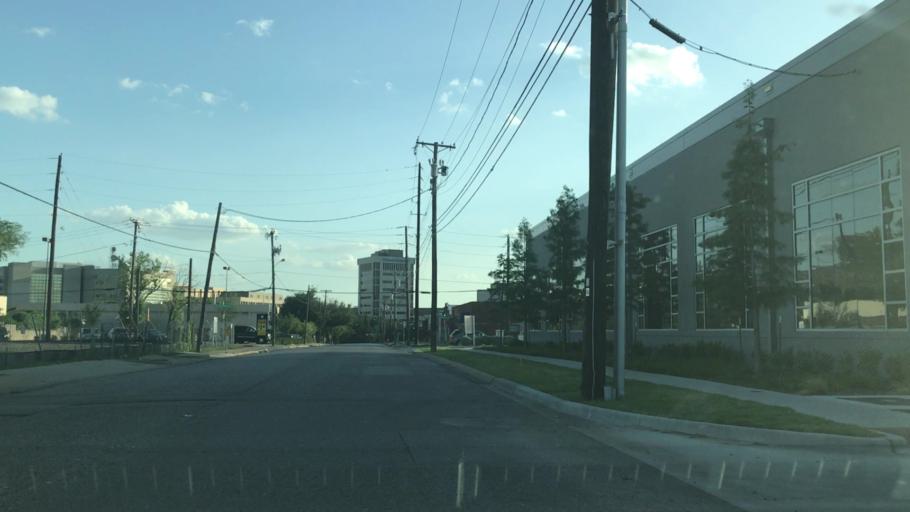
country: US
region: Texas
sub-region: Dallas County
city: Dallas
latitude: 32.8158
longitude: -96.8370
